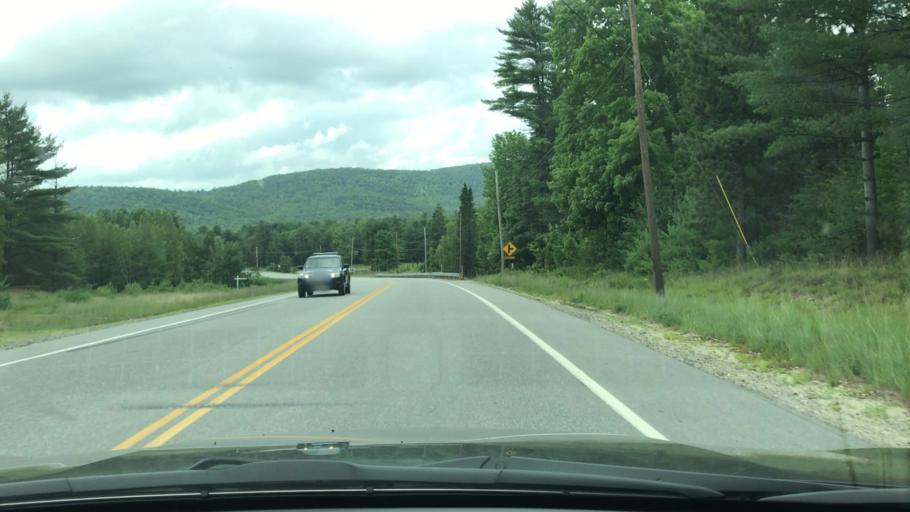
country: US
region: Maine
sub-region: Oxford County
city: Bethel
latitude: 44.4141
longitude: -70.7337
